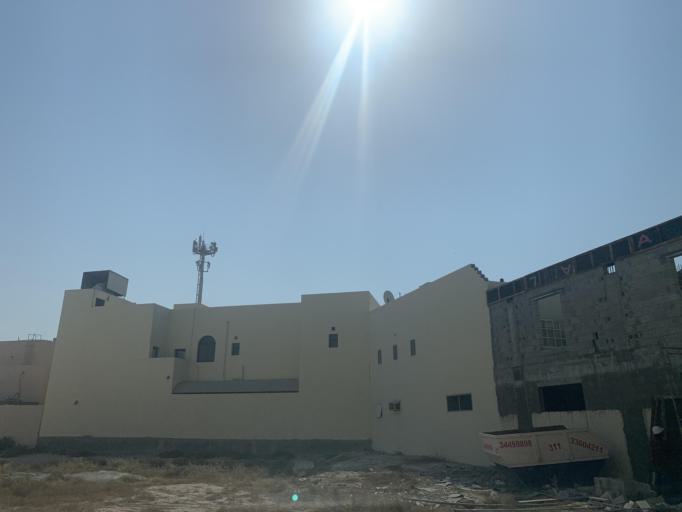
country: BH
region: Central Governorate
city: Madinat Hamad
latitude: 26.1384
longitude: 50.4947
